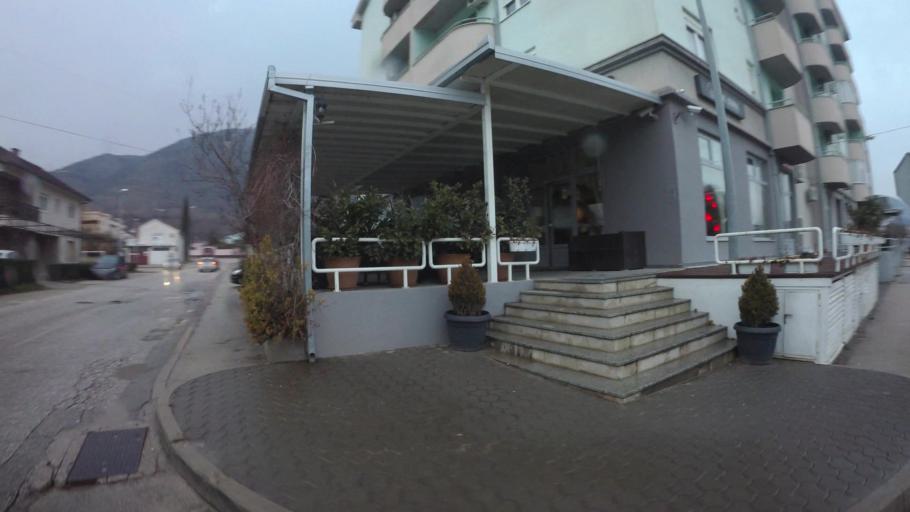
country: BA
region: Federation of Bosnia and Herzegovina
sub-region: Hercegovacko-Bosanski Kanton
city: Mostar
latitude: 43.3542
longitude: 17.7964
